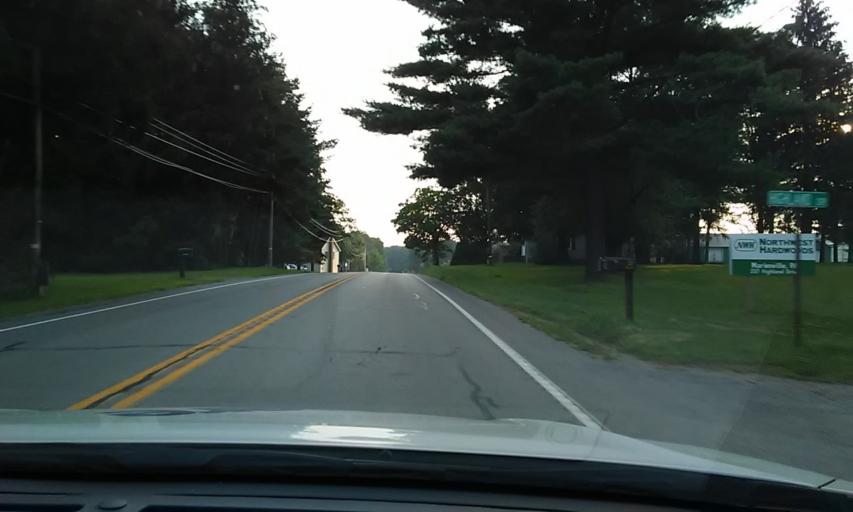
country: US
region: Pennsylvania
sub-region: Forest County
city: Marienville
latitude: 41.4556
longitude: -79.1530
